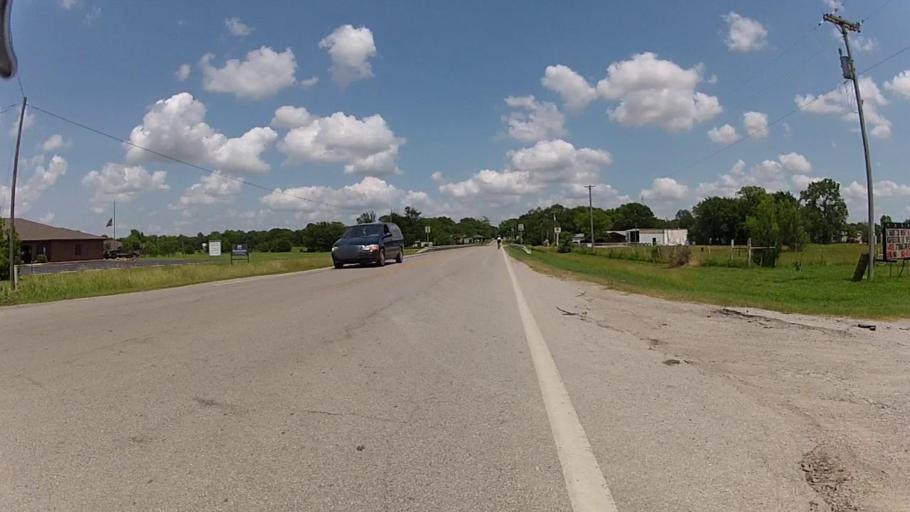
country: US
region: Kansas
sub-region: Labette County
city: Altamont
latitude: 37.1930
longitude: -95.3021
